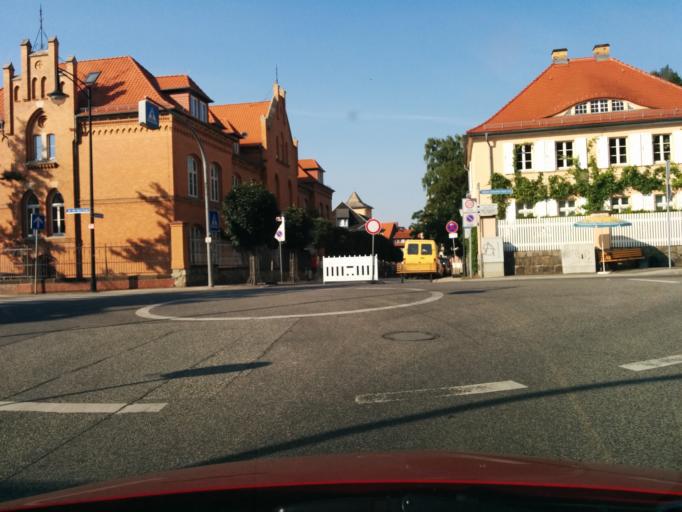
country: DE
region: Saxony-Anhalt
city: Wernigerode
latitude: 51.8310
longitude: 10.7846
